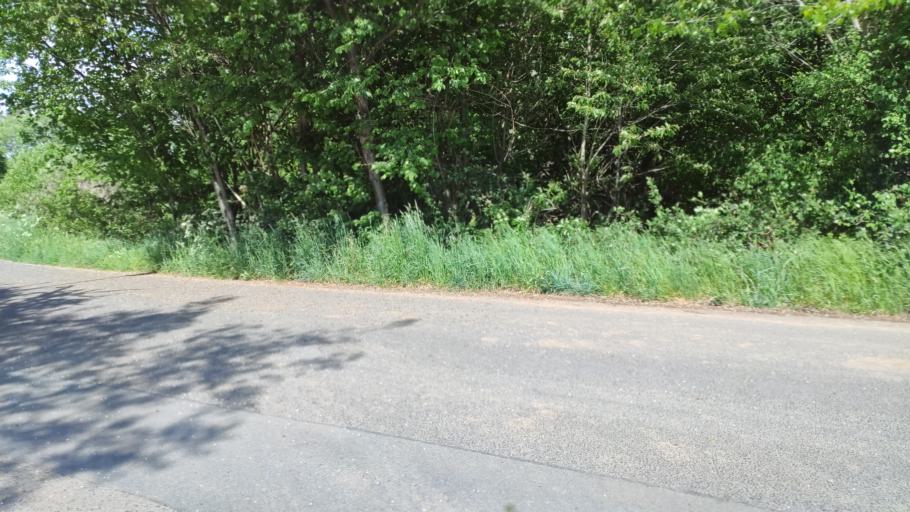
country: DE
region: North Rhine-Westphalia
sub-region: Regierungsbezirk Dusseldorf
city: Neubrueck
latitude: 51.1497
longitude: 6.6651
